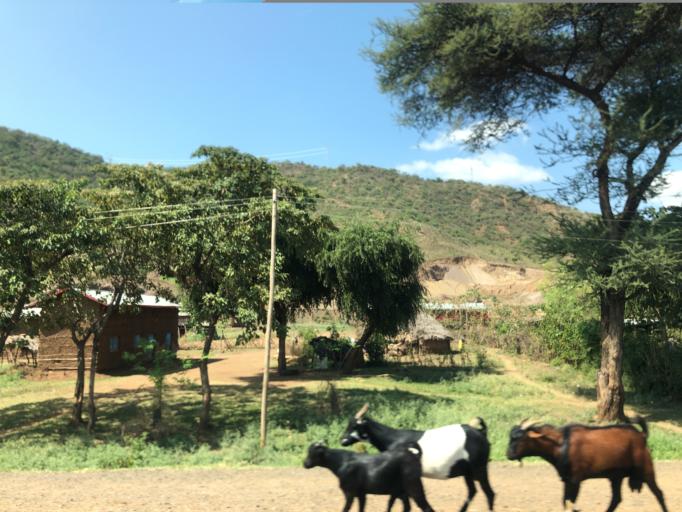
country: ET
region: Southern Nations, Nationalities, and People's Region
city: Gidole
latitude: 5.8165
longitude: 37.4568
